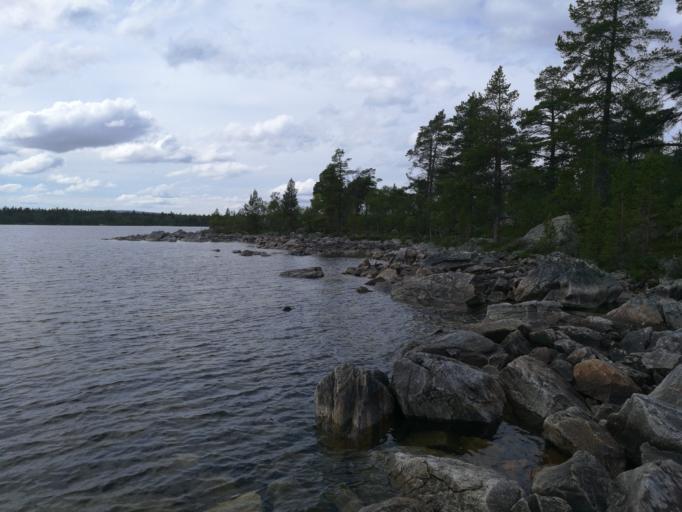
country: NO
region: Sor-Trondelag
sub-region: Roros
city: Roros
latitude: 62.4093
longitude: 11.9567
